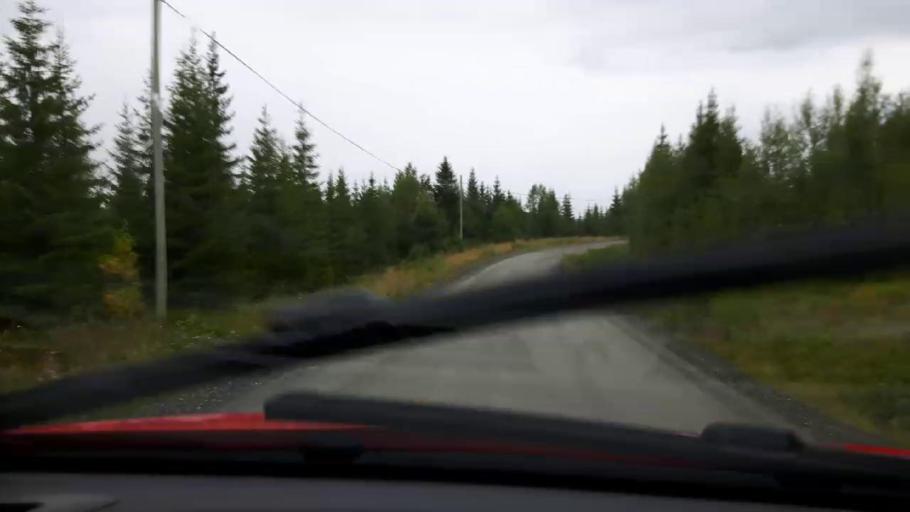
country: SE
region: Jaemtland
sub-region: Are Kommun
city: Are
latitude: 63.4214
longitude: 12.8224
